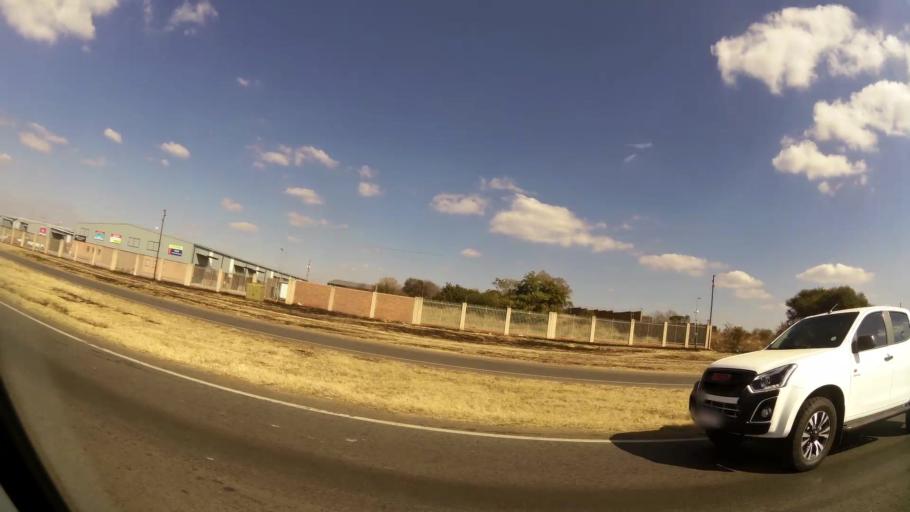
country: ZA
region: Gauteng
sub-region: City of Tshwane Metropolitan Municipality
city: Pretoria
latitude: -25.7487
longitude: 28.3614
